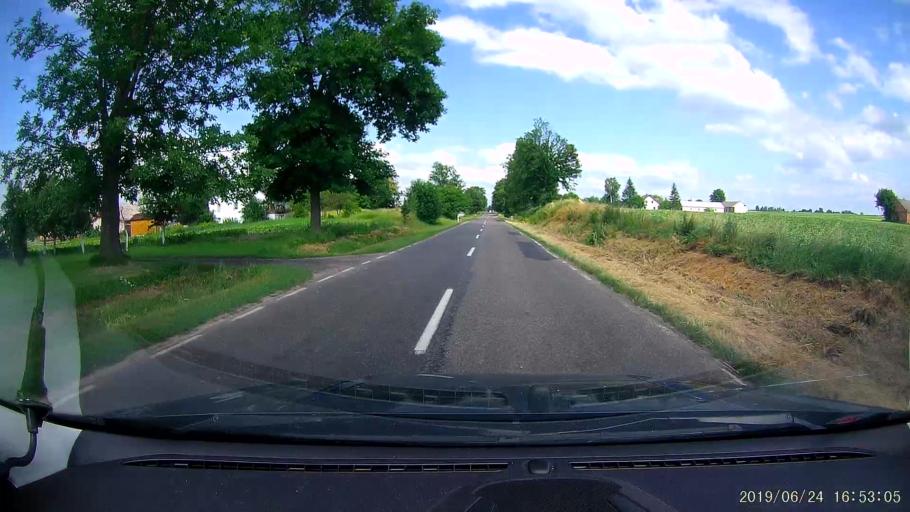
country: PL
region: Lublin Voivodeship
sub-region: Powiat tomaszowski
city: Telatyn
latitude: 50.5356
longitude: 23.7923
